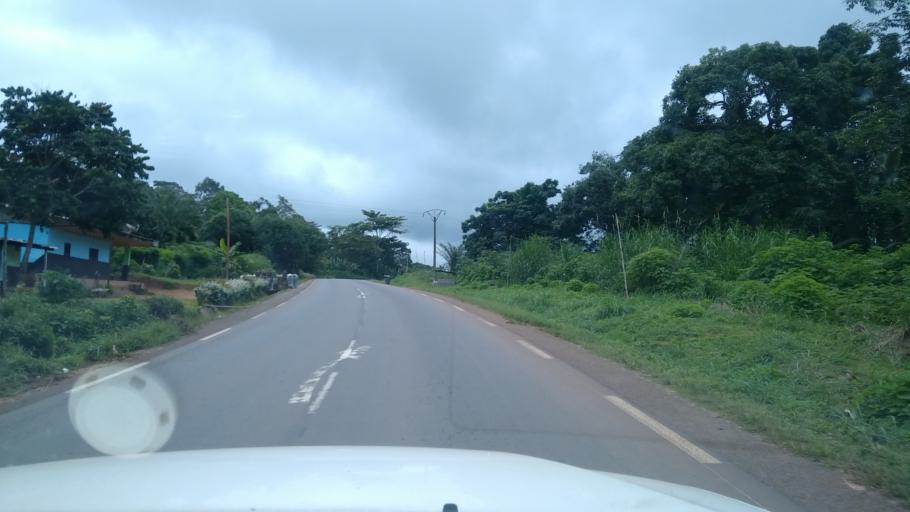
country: CM
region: Centre
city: Mbalmayo
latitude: 3.6013
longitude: 11.5261
